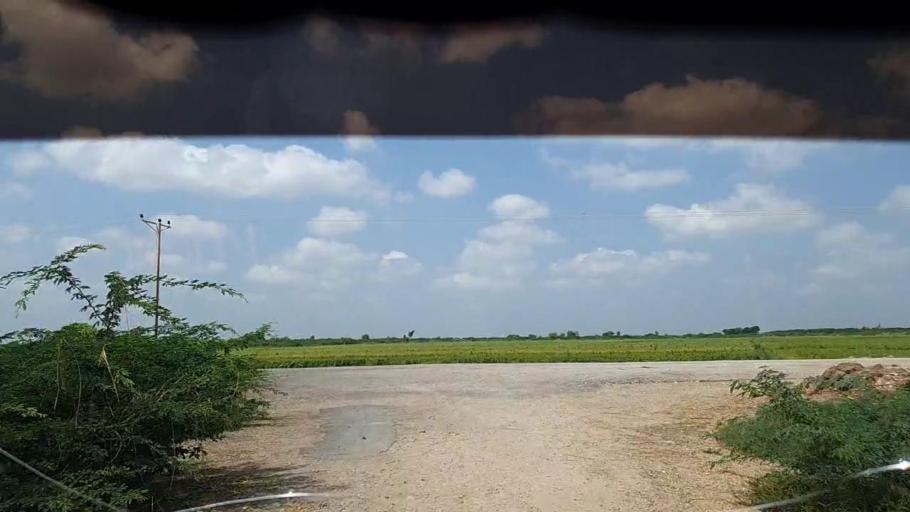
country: PK
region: Sindh
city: Kadhan
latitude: 24.5958
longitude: 68.9630
